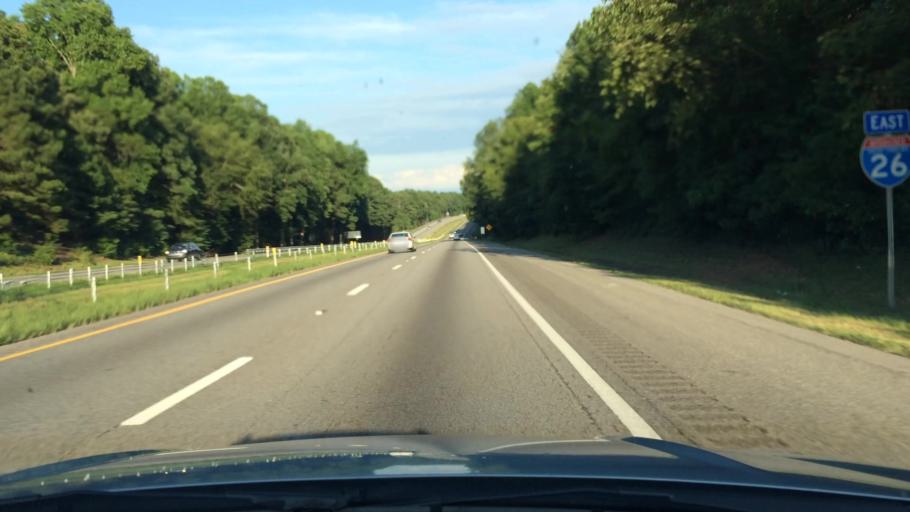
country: US
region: South Carolina
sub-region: Newberry County
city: Prosperity
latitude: 34.2360
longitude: -81.4519
